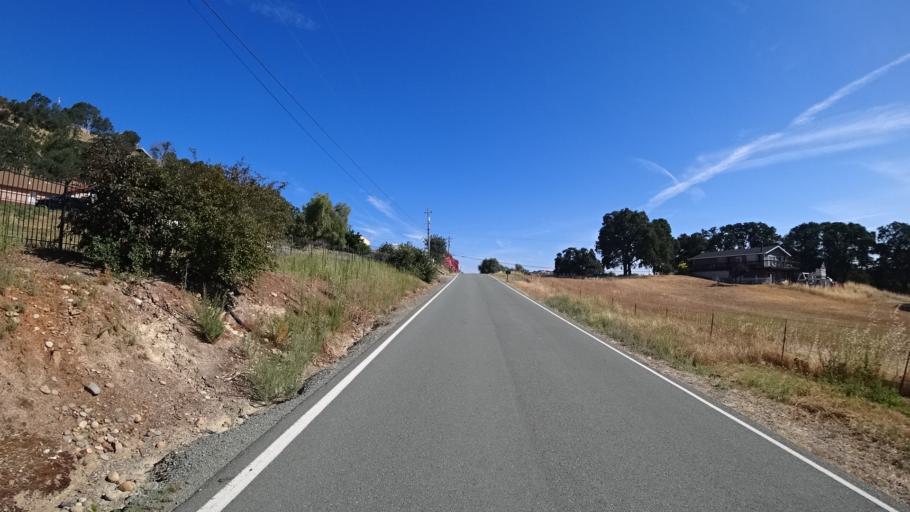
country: US
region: California
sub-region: Calaveras County
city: Rancho Calaveras
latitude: 38.1604
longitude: -120.8539
